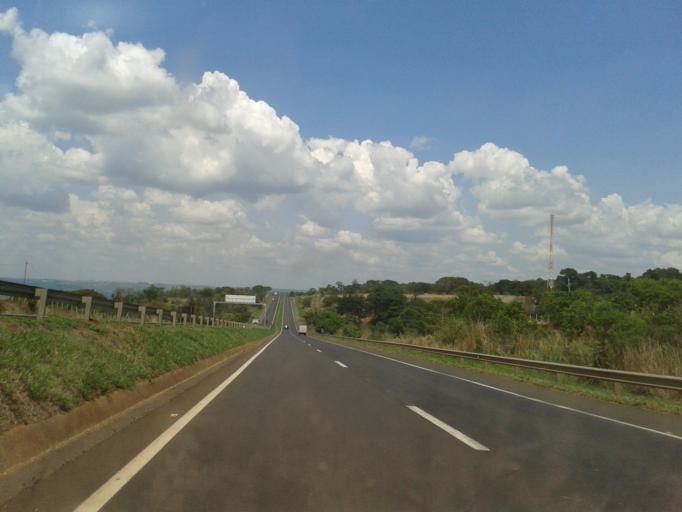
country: BR
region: Minas Gerais
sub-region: Araguari
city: Araguari
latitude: -18.7055
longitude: -48.1910
